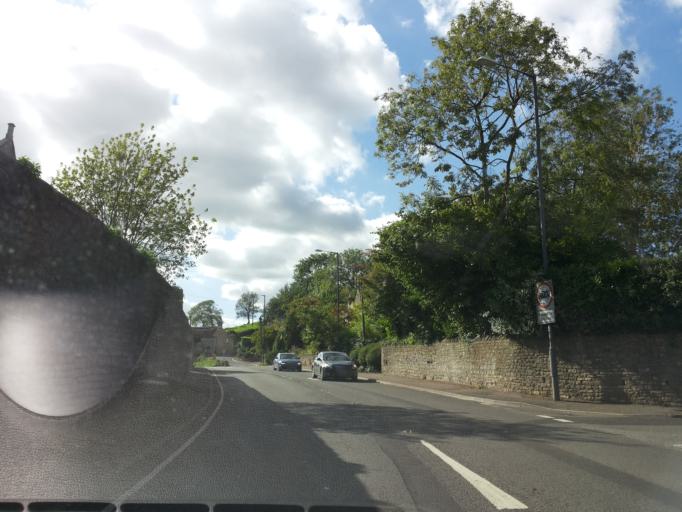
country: GB
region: England
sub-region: Bath and North East Somerset
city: Corston
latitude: 51.3862
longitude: -2.4403
